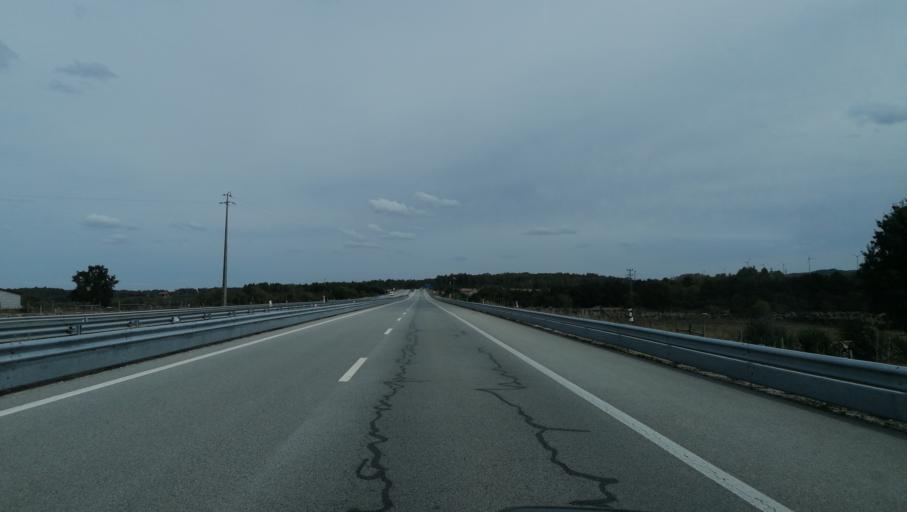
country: PT
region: Vila Real
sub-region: Vila Pouca de Aguiar
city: Vila Pouca de Aguiar
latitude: 41.4925
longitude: -7.6780
